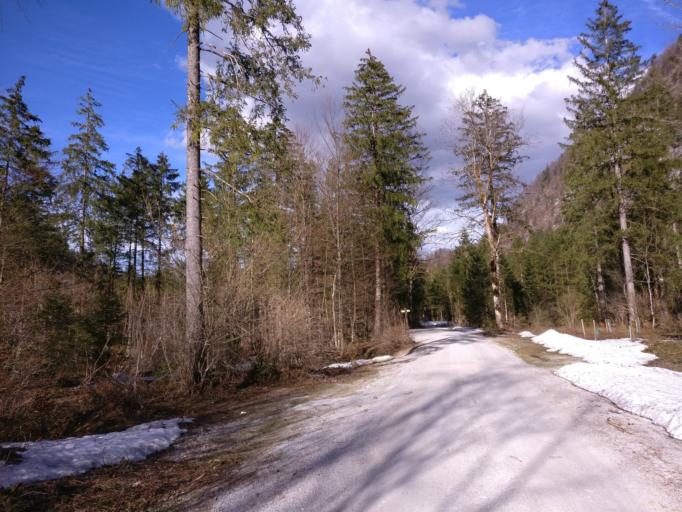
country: AT
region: Salzburg
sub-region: Politischer Bezirk Hallein
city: Golling an der Salzach
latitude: 47.5766
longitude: 13.1405
